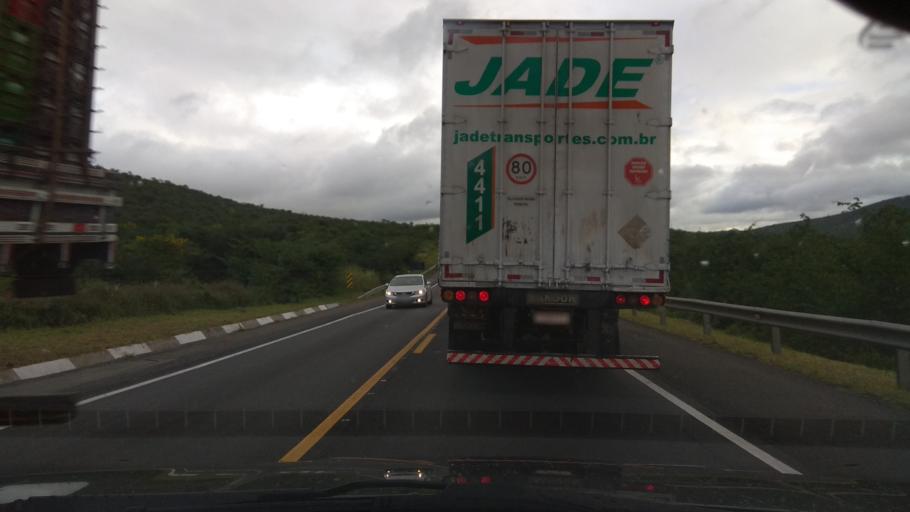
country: BR
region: Bahia
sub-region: Santa Ines
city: Santa Ines
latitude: -13.2812
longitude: -40.0174
